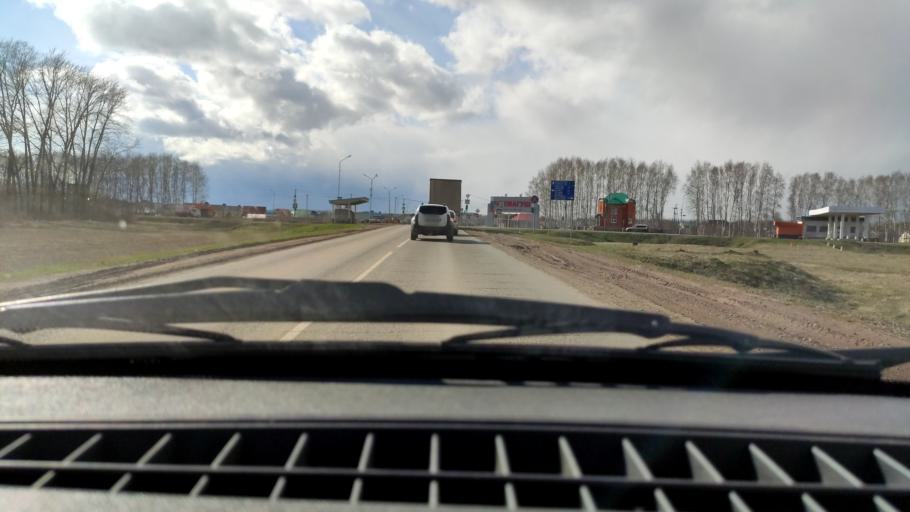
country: RU
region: Bashkortostan
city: Chekmagush
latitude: 55.1297
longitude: 54.6871
